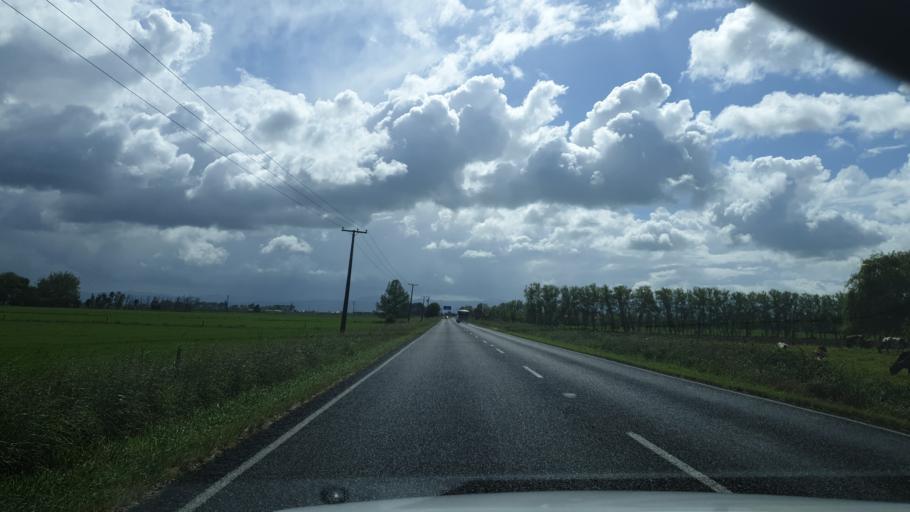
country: NZ
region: Waikato
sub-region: Hauraki District
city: Paeroa
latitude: -37.5123
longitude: 175.5169
